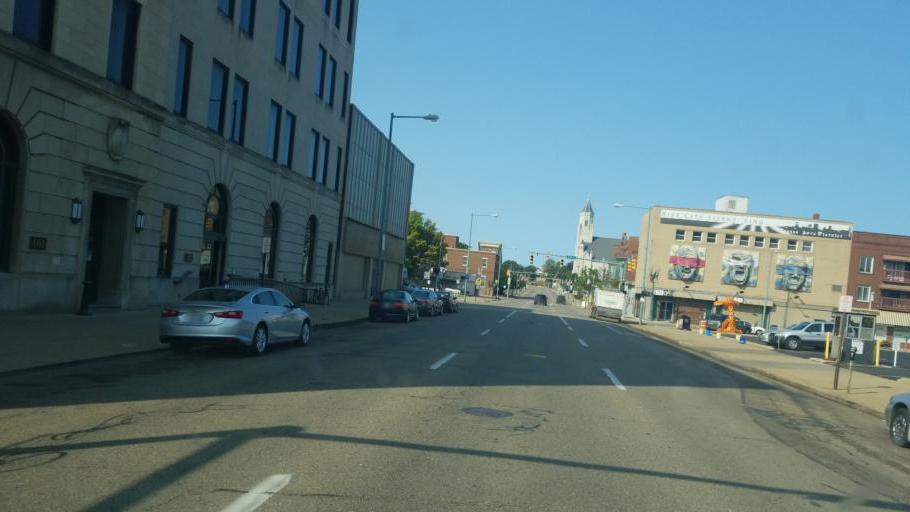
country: US
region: Ohio
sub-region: Stark County
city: Canton
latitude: 40.8010
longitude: -81.3757
